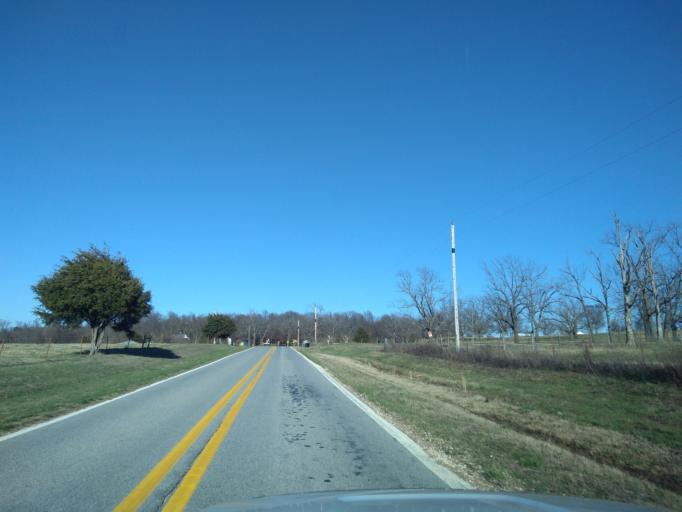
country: US
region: Arkansas
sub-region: Washington County
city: Lincoln
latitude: 35.9357
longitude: -94.3797
